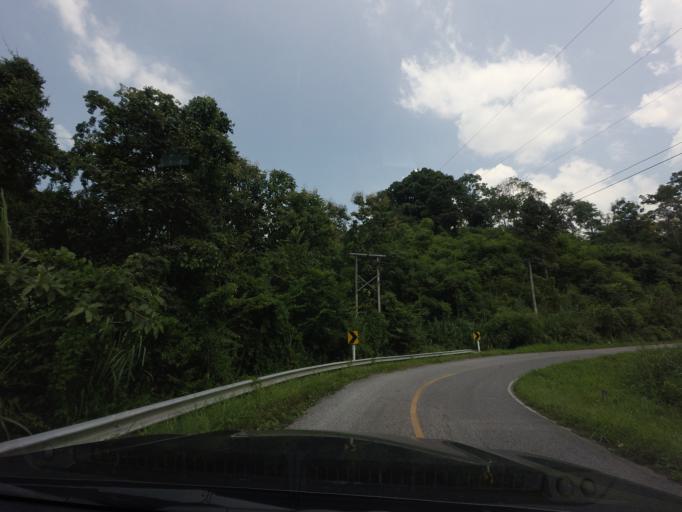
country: TH
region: Loei
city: Na Haeo
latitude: 17.6969
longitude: 100.9349
